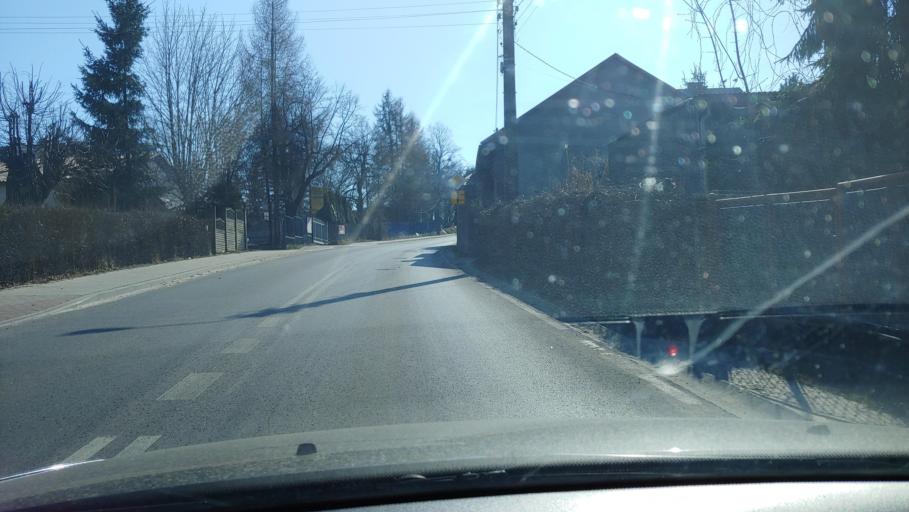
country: PL
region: Lesser Poland Voivodeship
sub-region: Powiat chrzanowski
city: Trzebinia
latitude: 50.1762
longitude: 19.4529
